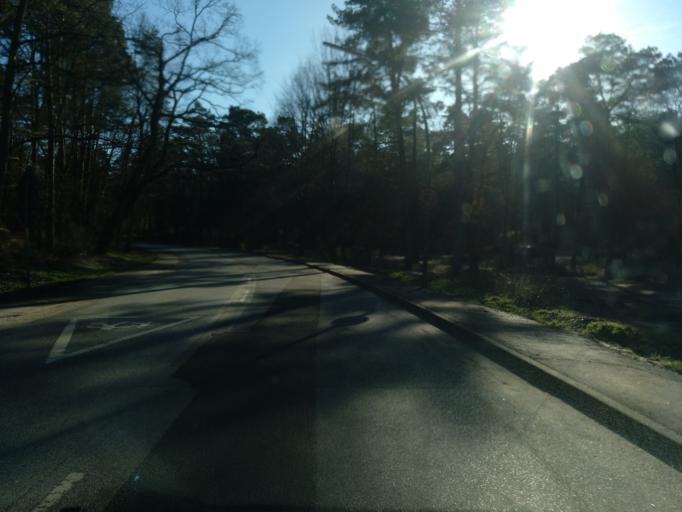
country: DE
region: Hamburg
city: Harburg
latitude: 53.4606
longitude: 9.8920
